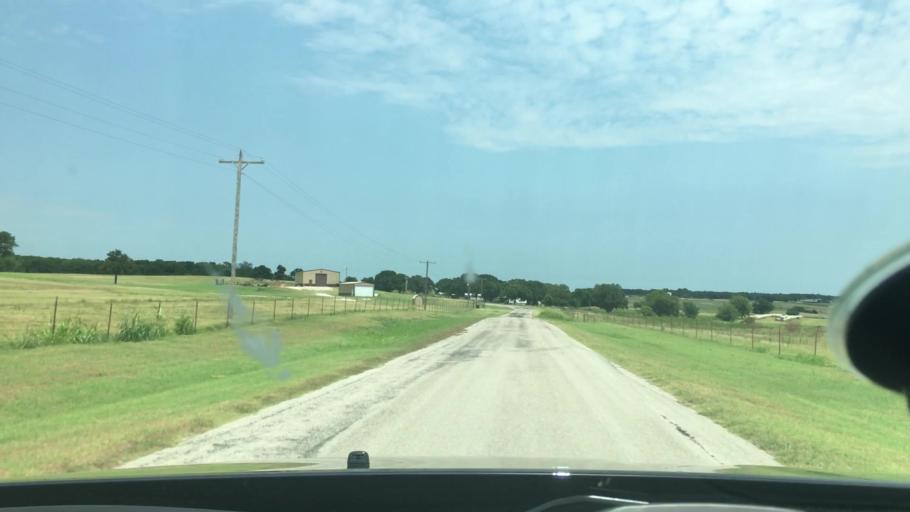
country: US
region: Texas
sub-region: Cooke County
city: Muenster
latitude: 33.8881
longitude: -97.3539
